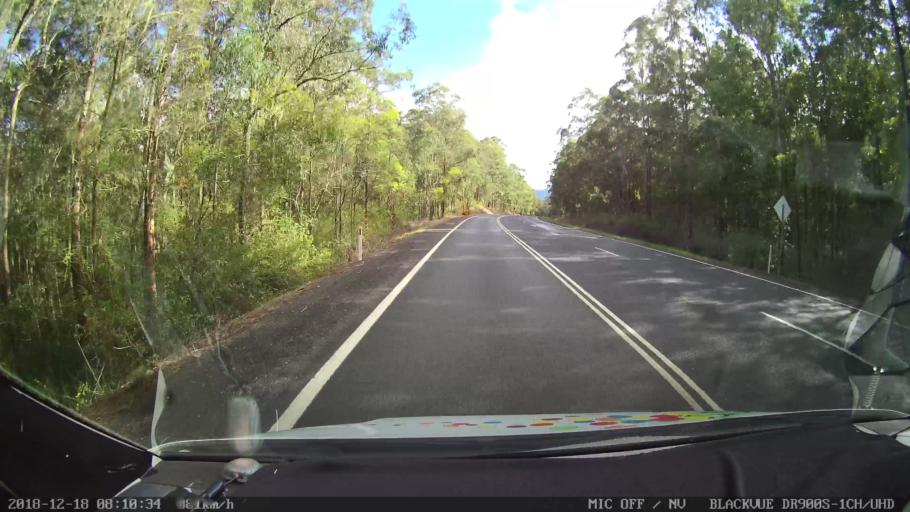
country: AU
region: New South Wales
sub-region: Kyogle
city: Kyogle
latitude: -28.3601
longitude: 152.6626
